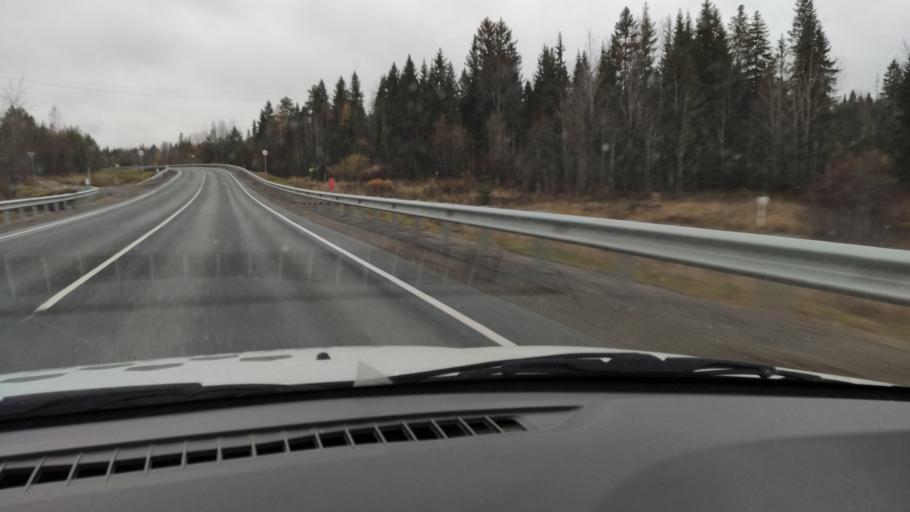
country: RU
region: Kirov
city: Omutninsk
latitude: 58.6944
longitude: 52.1285
